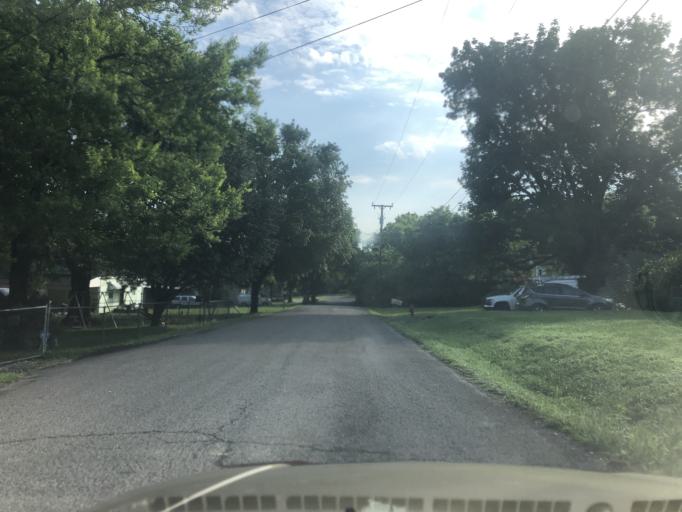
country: US
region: Tennessee
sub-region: Davidson County
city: Lakewood
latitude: 36.2465
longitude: -86.7114
